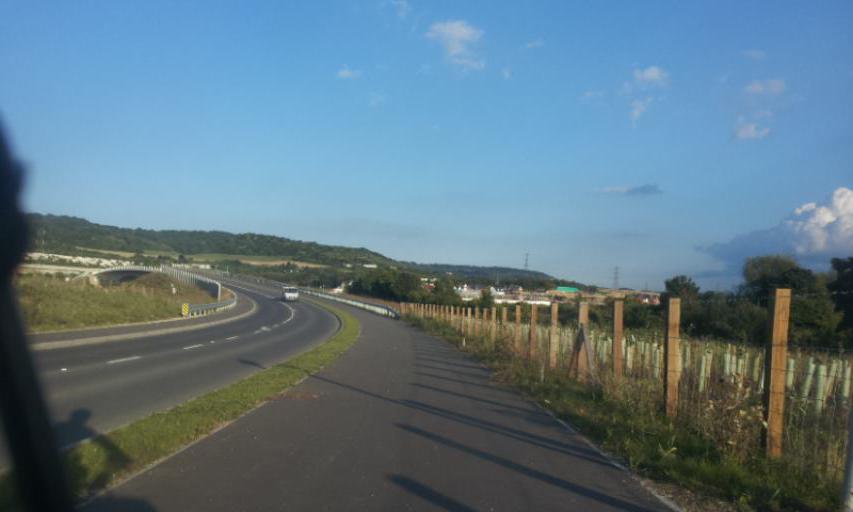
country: GB
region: England
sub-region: Medway
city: Halling
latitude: 51.3415
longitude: 0.4491
